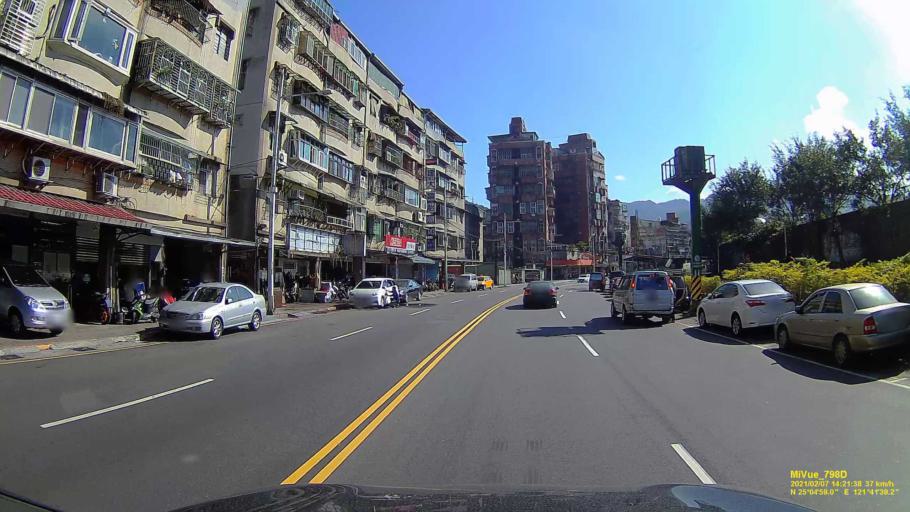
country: TW
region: Taiwan
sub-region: Keelung
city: Keelung
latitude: 25.0829
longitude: 121.6943
